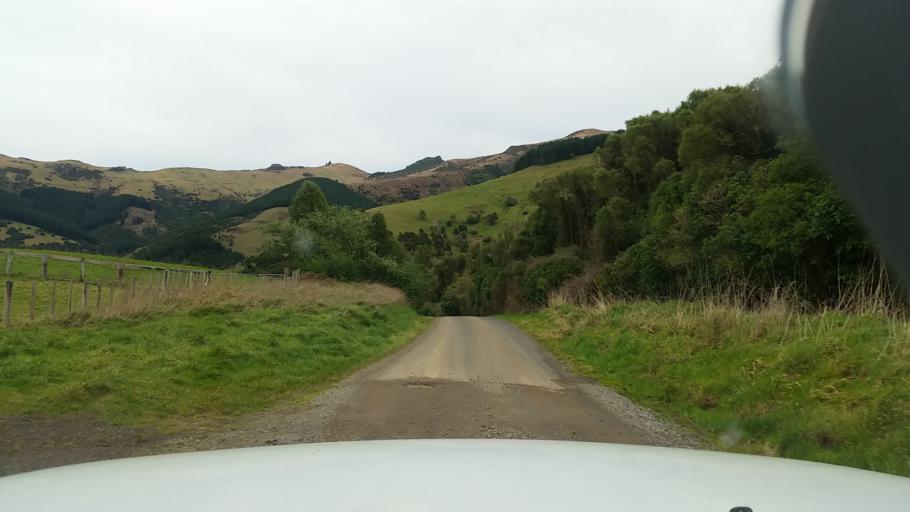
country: NZ
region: Canterbury
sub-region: Christchurch City
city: Christchurch
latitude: -43.7309
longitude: 172.7994
